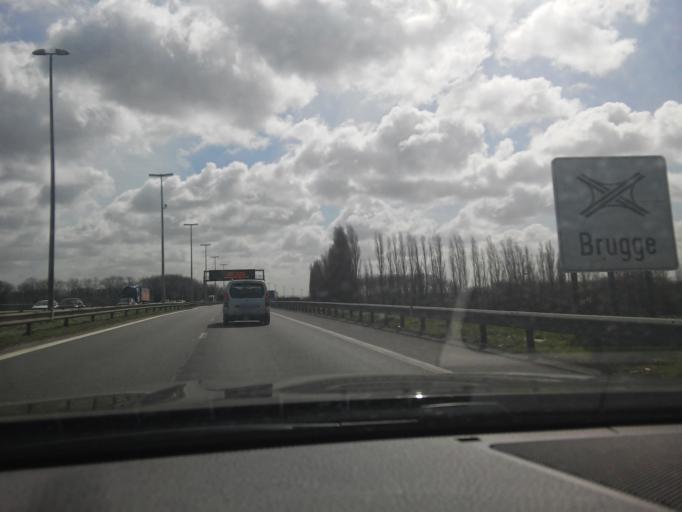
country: BE
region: Flanders
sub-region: Provincie West-Vlaanderen
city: Oostkamp
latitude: 51.1679
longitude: 3.2100
